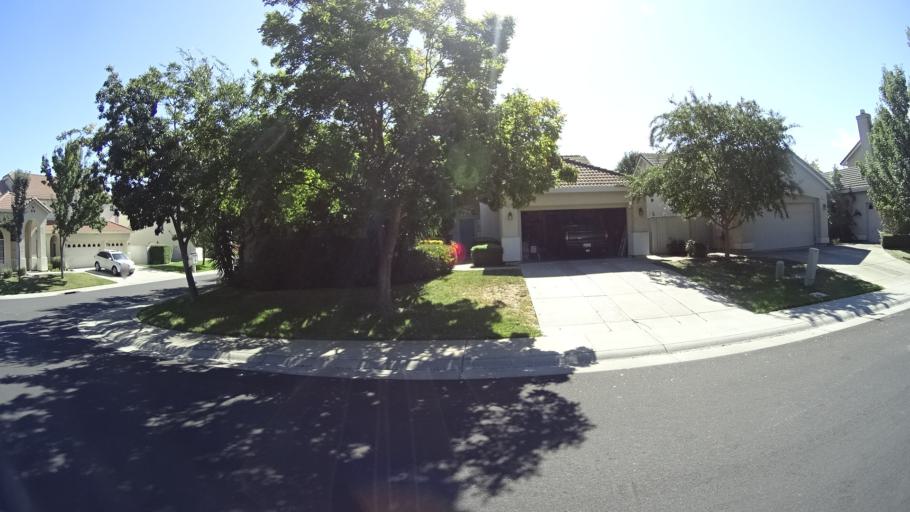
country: US
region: California
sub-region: Sacramento County
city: Laguna
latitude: 38.4181
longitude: -121.4787
